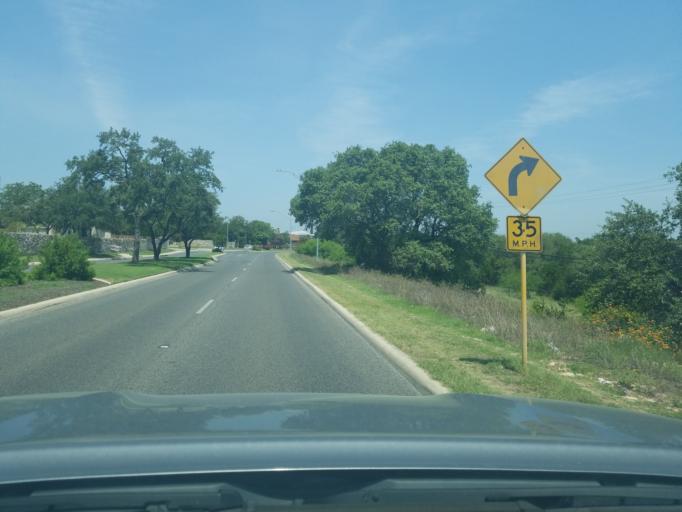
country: US
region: Texas
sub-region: Bexar County
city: Hollywood Park
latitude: 29.6460
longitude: -98.4934
